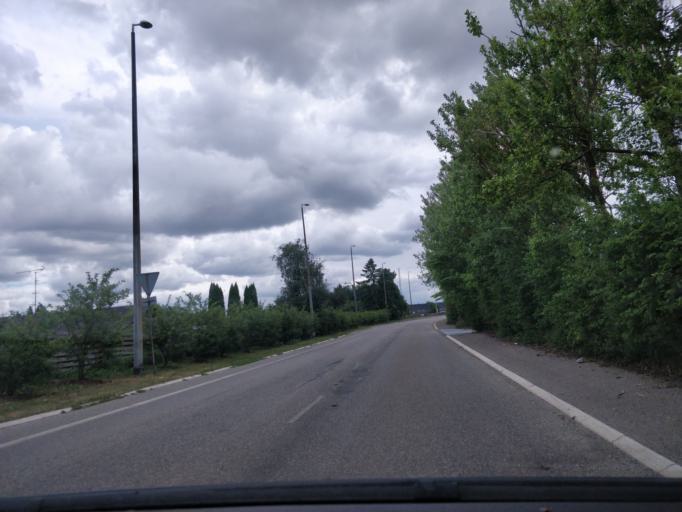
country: DK
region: Capital Region
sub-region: Herlev Kommune
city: Herlev
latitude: 55.7064
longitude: 12.4296
